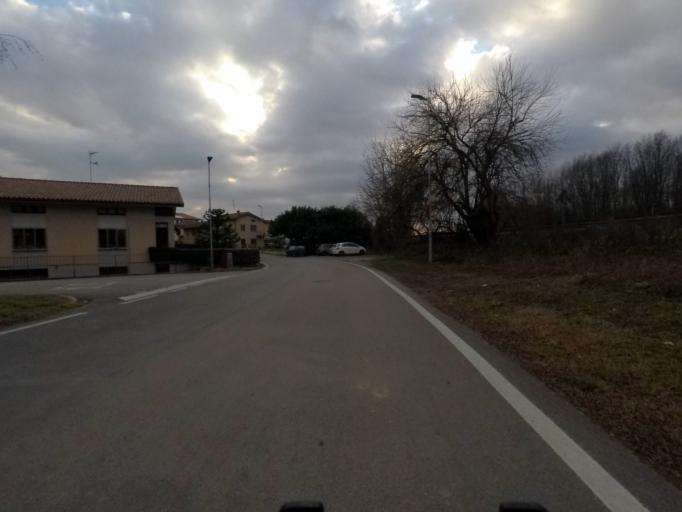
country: IT
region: Friuli Venezia Giulia
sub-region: Provincia di Udine
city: Colugna
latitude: 46.1017
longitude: 13.2051
